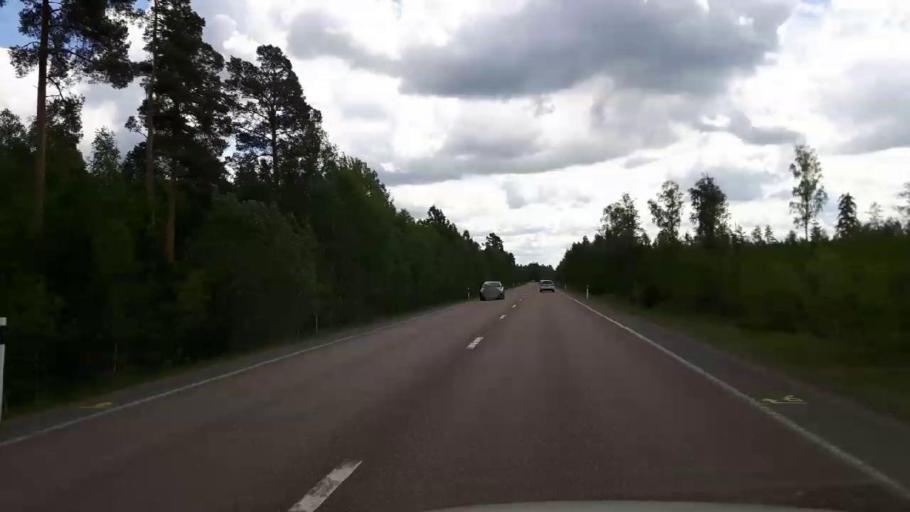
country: SE
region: Dalarna
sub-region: Saters Kommun
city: Saeter
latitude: 60.4939
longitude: 15.7601
